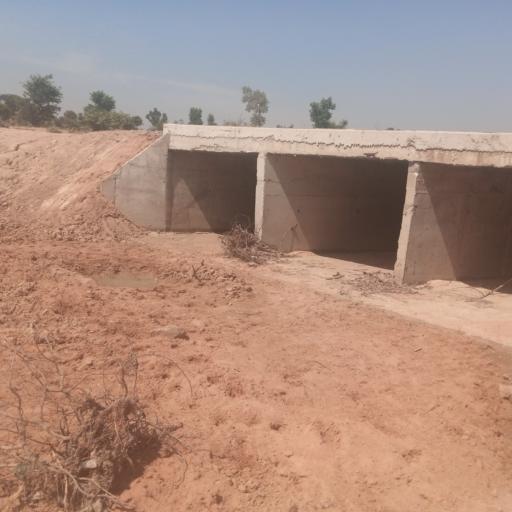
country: NG
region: Adamawa
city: Yola
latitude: 9.1910
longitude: 12.4148
